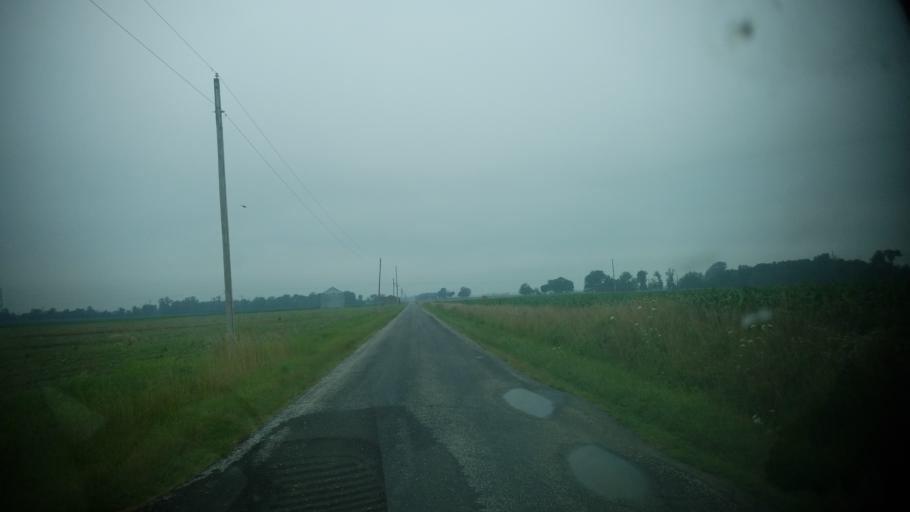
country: US
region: Illinois
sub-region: Clay County
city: Flora
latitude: 38.5736
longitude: -88.3984
